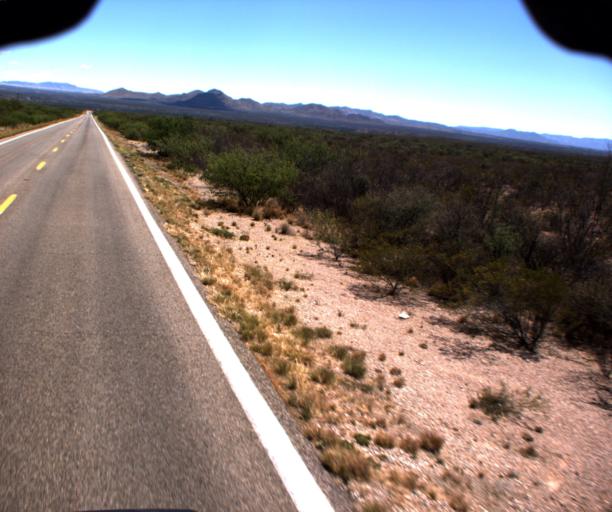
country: US
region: Arizona
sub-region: Cochise County
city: Huachuca City
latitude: 31.7198
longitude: -110.2359
